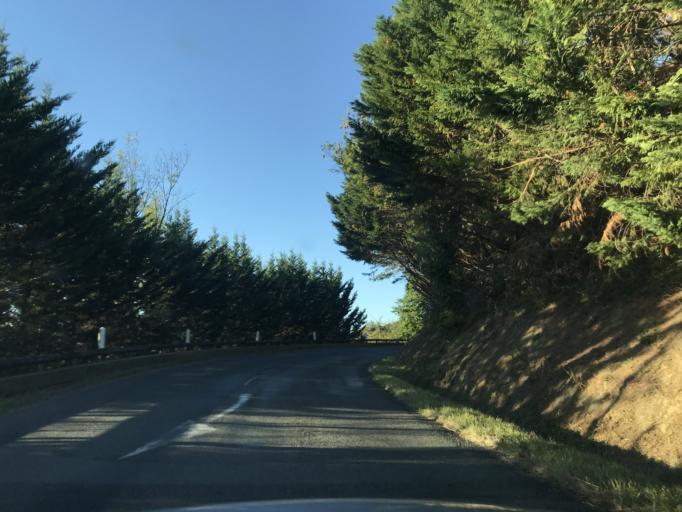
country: FR
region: Aquitaine
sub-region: Departement de la Gironde
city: Mouliets-et-Villemartin
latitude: 44.8795
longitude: -0.0476
